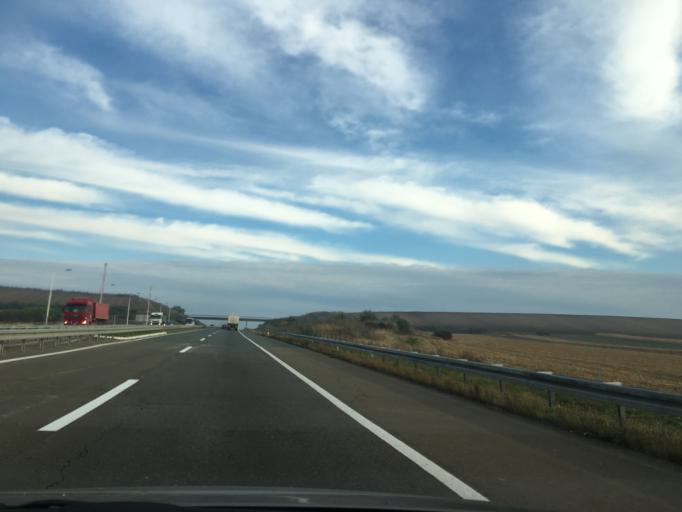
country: RS
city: Beska
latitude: 45.1511
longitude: 20.0830
